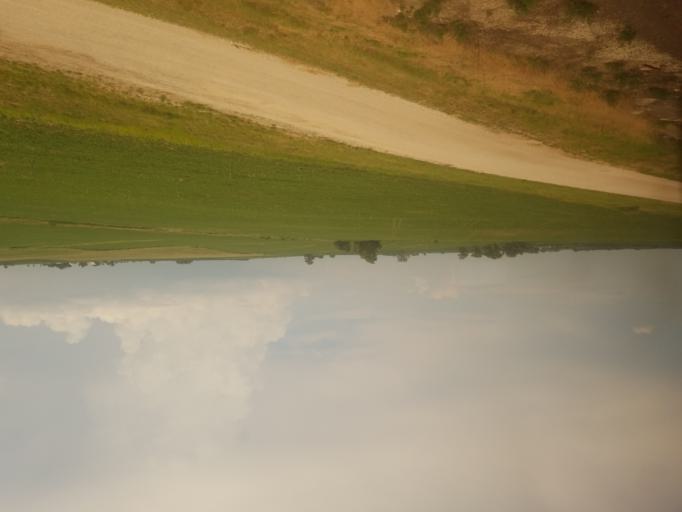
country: US
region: Illinois
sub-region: Henry County
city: Galva
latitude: 41.0878
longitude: -90.2033
